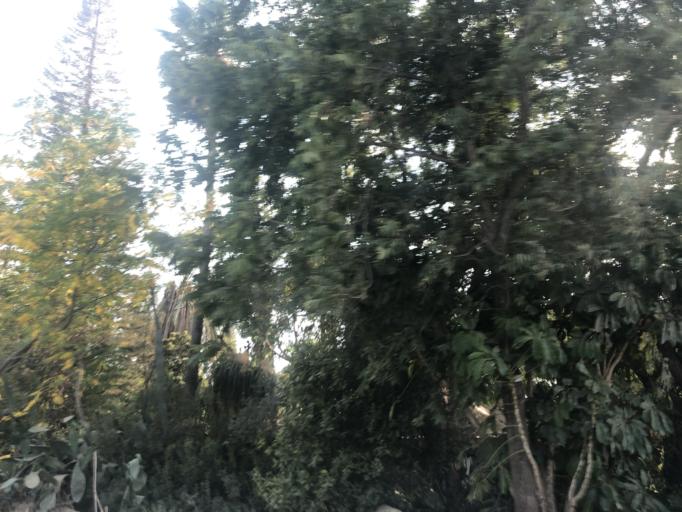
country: IL
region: Central District
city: Rosh Ha'Ayin
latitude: 32.0855
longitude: 34.9394
